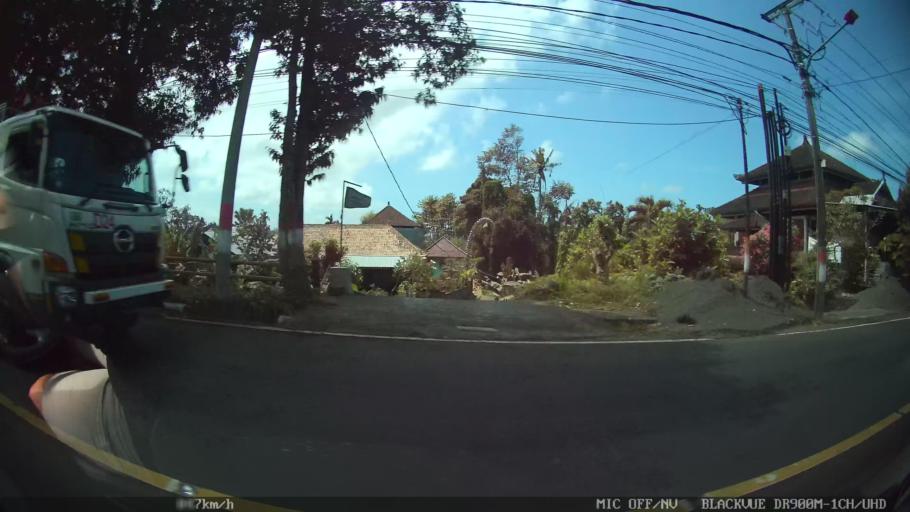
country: ID
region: Bali
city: Banjar Desa
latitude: -8.5836
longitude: 115.2822
